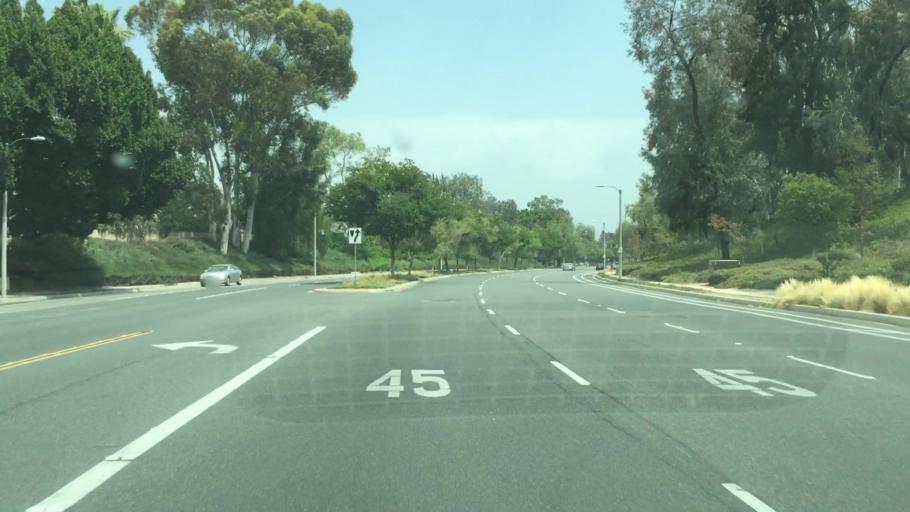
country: US
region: California
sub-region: San Bernardino County
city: Chino Hills
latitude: 34.0074
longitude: -117.7388
